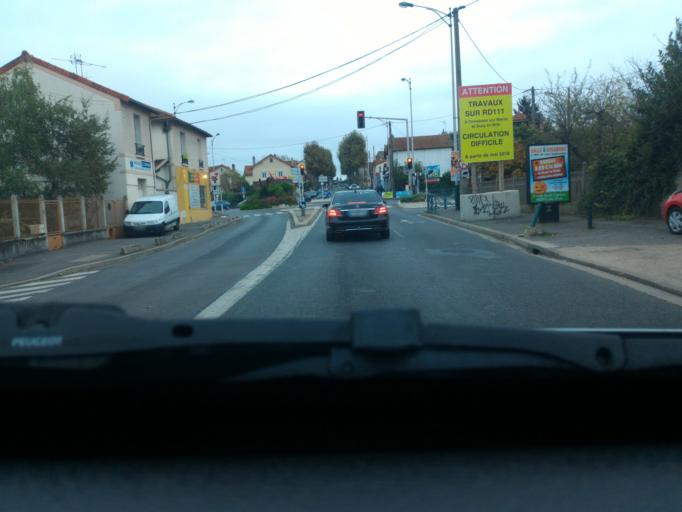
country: FR
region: Ile-de-France
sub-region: Departement du Val-de-Marne
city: Boissy-Saint-Leger
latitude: 48.7744
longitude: 2.5100
